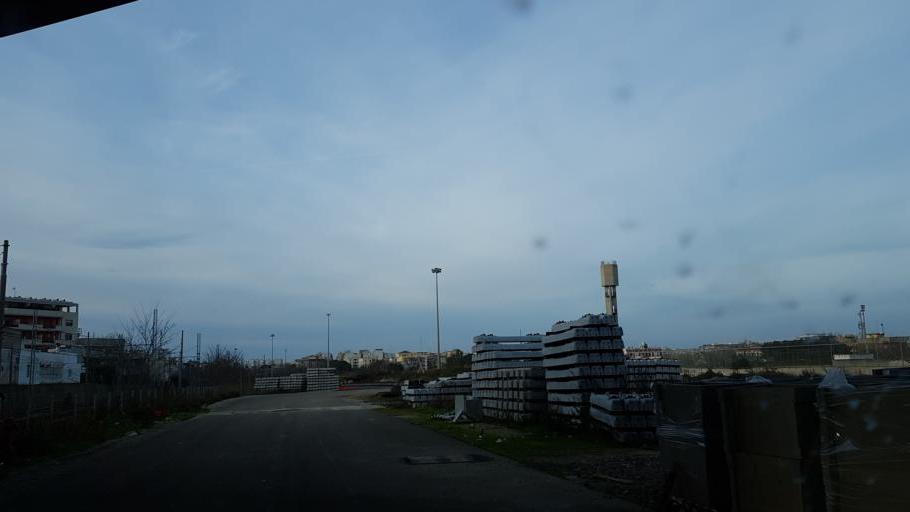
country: IT
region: Apulia
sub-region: Provincia di Brindisi
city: Brindisi
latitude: 40.6264
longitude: 17.9452
